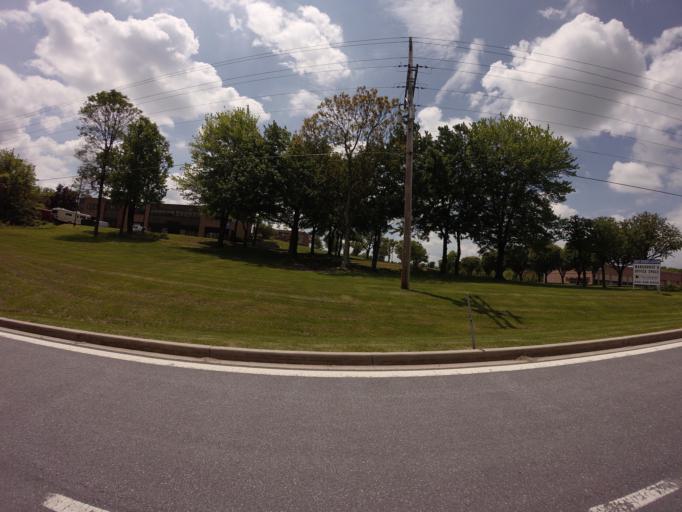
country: US
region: Maryland
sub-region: Frederick County
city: Green Valley
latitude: 39.2912
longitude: -77.3140
